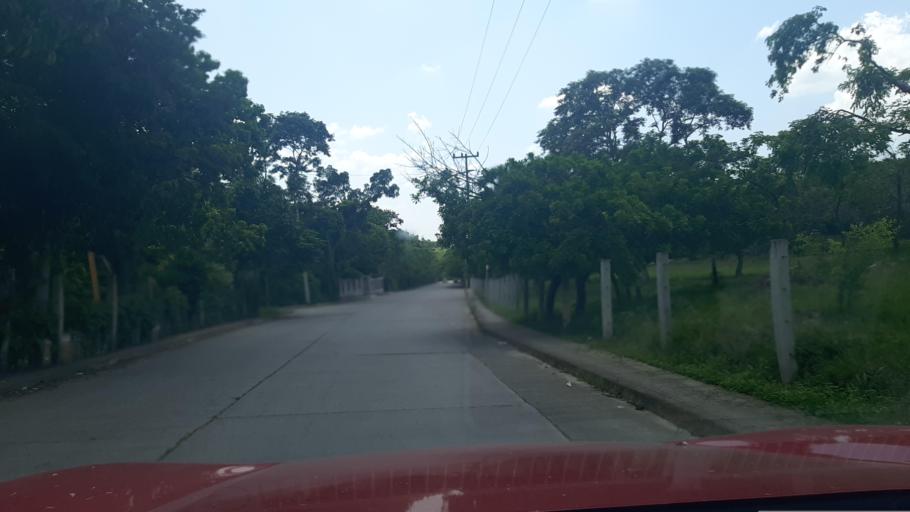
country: MX
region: Veracruz
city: Coatzintla
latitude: 20.4975
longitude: -97.4339
